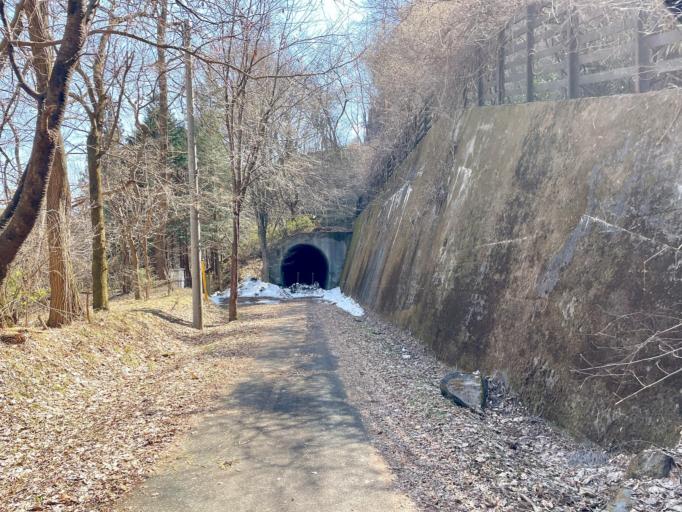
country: JP
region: Gunma
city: Nakanojomachi
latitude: 36.5649
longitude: 138.6360
